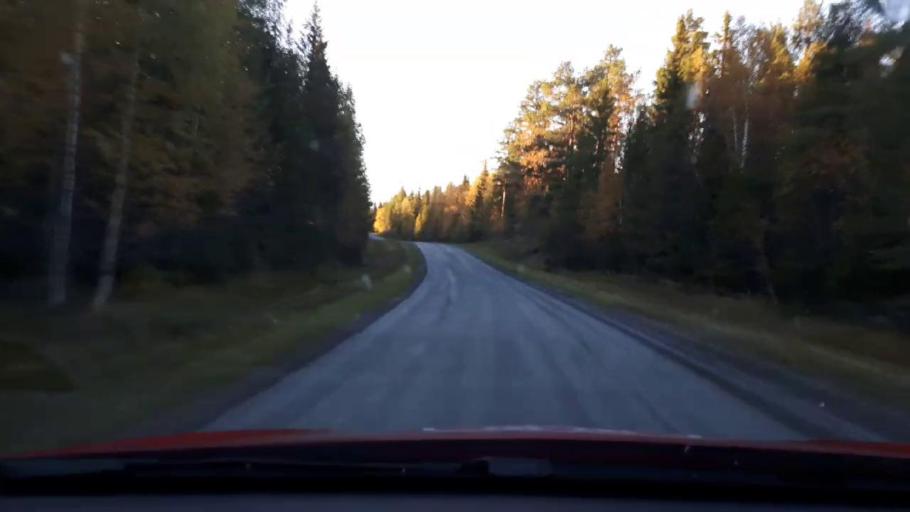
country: SE
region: Jaemtland
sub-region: Krokoms Kommun
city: Krokom
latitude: 63.4446
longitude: 14.4223
